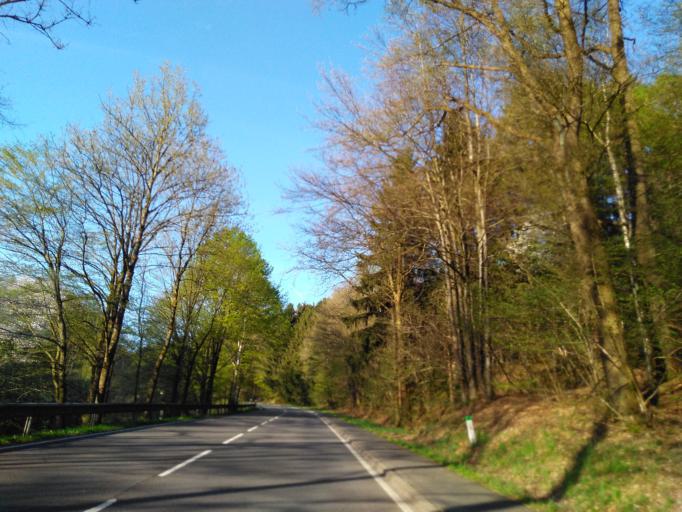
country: DE
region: North Rhine-Westphalia
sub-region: Regierungsbezirk Koln
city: Much
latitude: 50.9395
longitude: 7.4400
